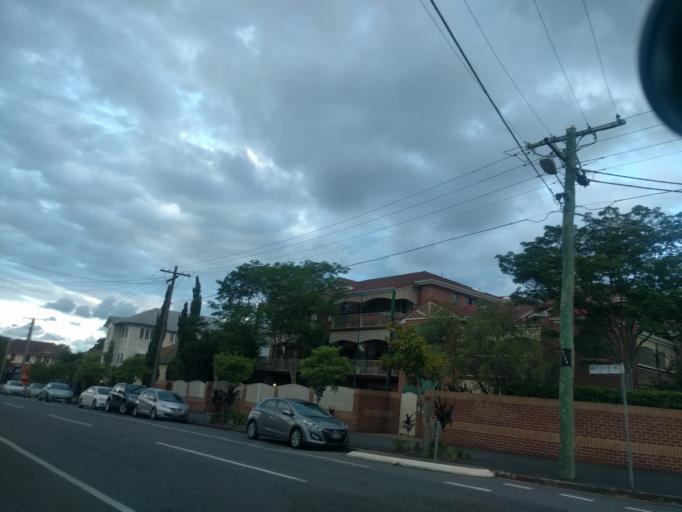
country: AU
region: Queensland
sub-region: Brisbane
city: Brisbane
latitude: -27.4680
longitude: 153.0453
